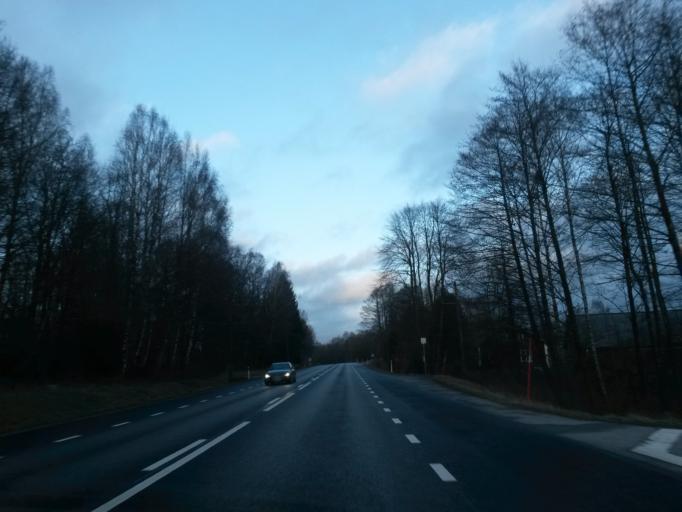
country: SE
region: Halland
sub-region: Halmstads Kommun
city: Aled
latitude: 56.7500
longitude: 12.9384
